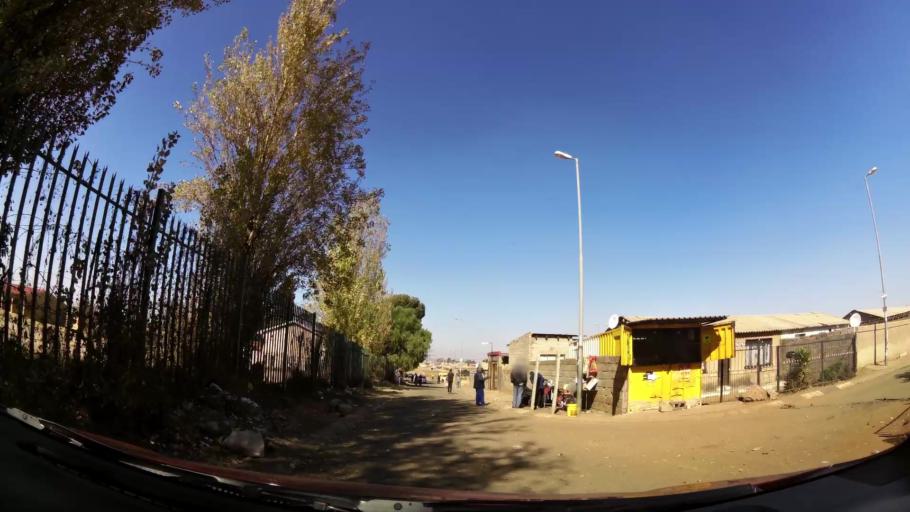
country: ZA
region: Gauteng
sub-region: City of Johannesburg Metropolitan Municipality
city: Soweto
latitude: -26.2397
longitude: 27.8432
